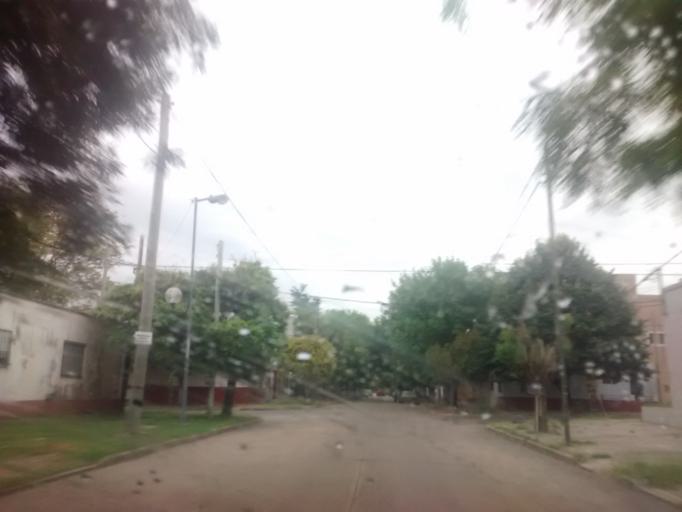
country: AR
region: Buenos Aires
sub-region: Partido de La Plata
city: La Plata
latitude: -34.9447
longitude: -57.9485
